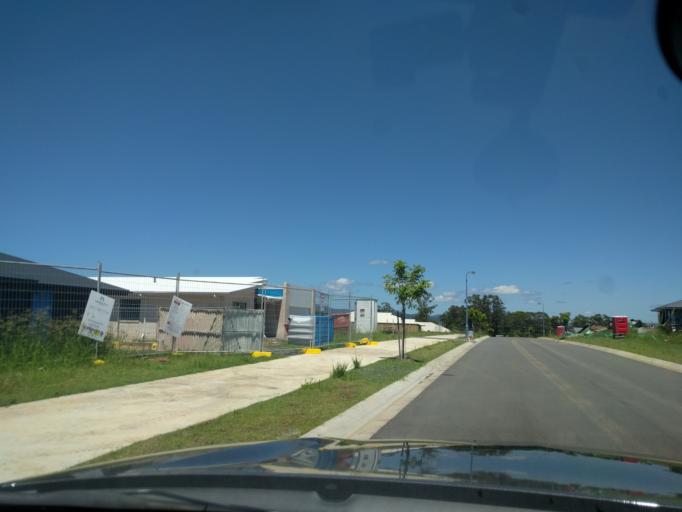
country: AU
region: Queensland
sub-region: Logan
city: Cedar Vale
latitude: -27.9885
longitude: 153.0122
